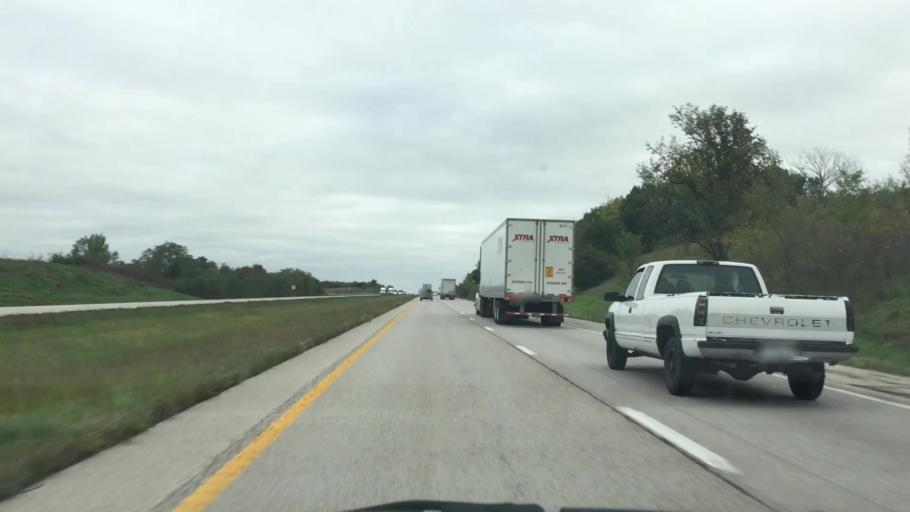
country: US
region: Missouri
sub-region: Clinton County
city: Cameron
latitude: 39.7014
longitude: -94.2271
